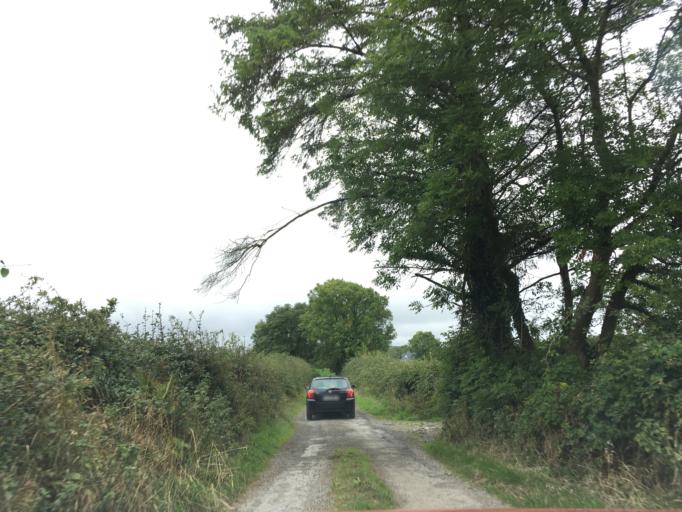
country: IE
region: Munster
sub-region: An Clar
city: Ennis
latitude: 52.7247
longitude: -9.0940
